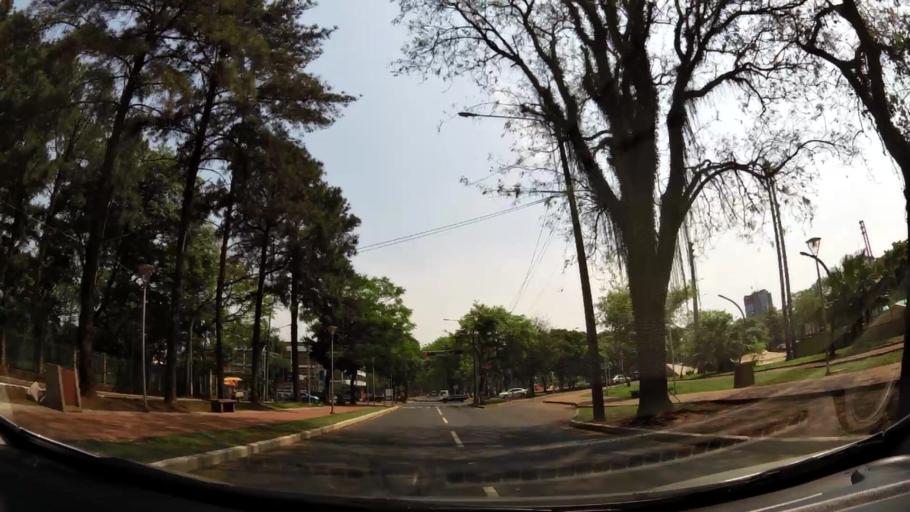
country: PY
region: Alto Parana
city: Ciudad del Este
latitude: -25.5210
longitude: -54.6130
